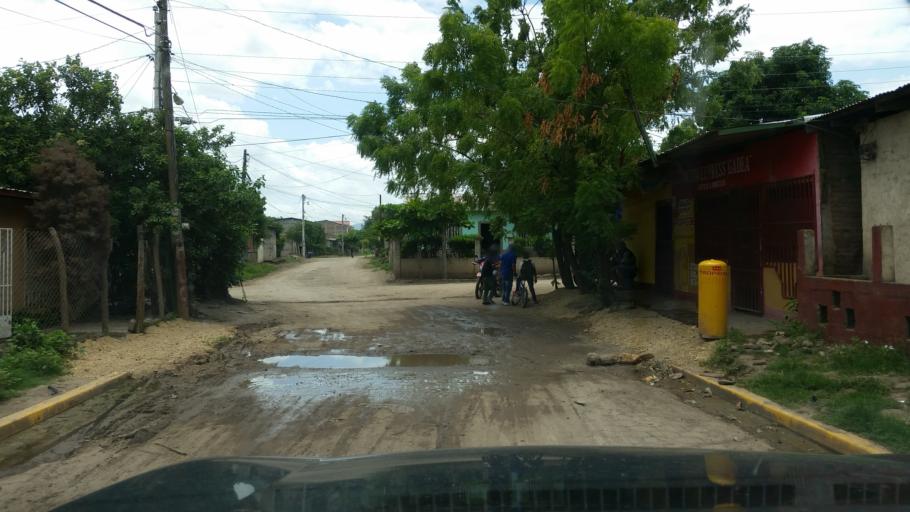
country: NI
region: Matagalpa
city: Ciudad Dario
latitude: 12.8591
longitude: -86.0915
